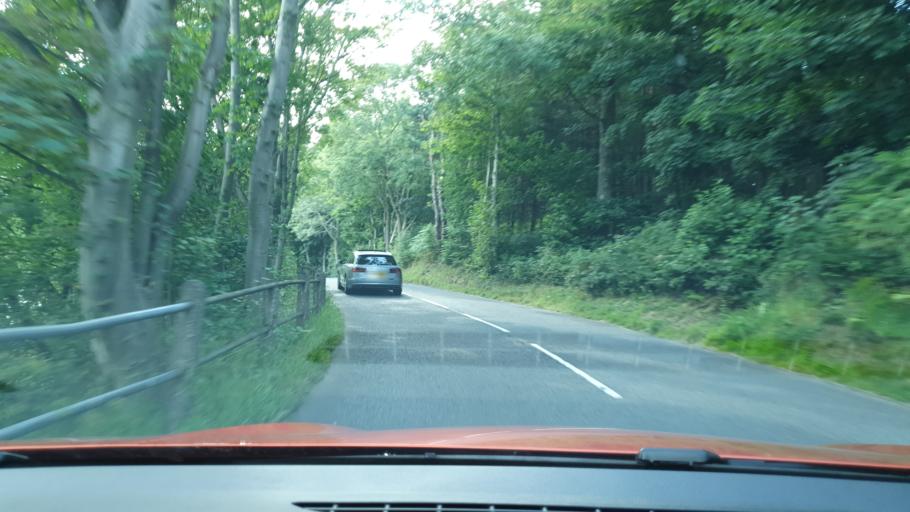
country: GB
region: England
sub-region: Cumbria
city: Ambleside
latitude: 54.5733
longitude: -2.9192
